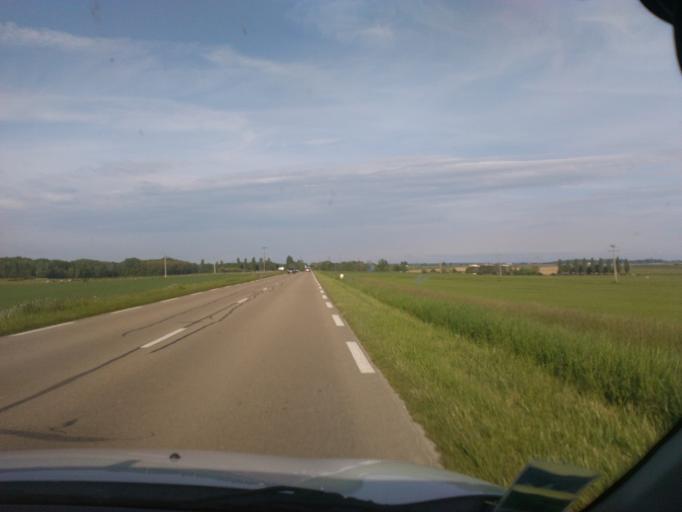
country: FR
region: Champagne-Ardenne
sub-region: Departement de l'Aube
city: Lusigny-sur-Barse
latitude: 48.2417
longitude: 4.3411
